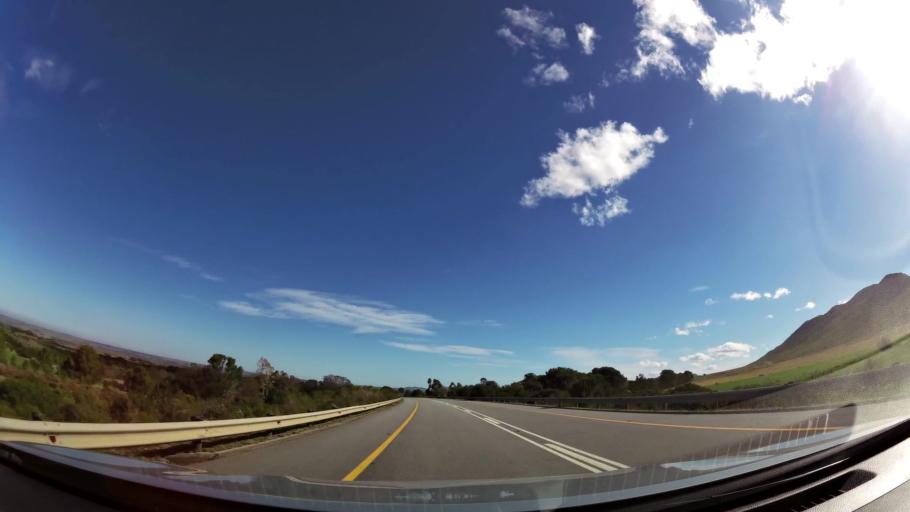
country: ZA
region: Eastern Cape
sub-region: Cacadu District Municipality
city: Kruisfontein
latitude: -33.9943
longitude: 24.6944
